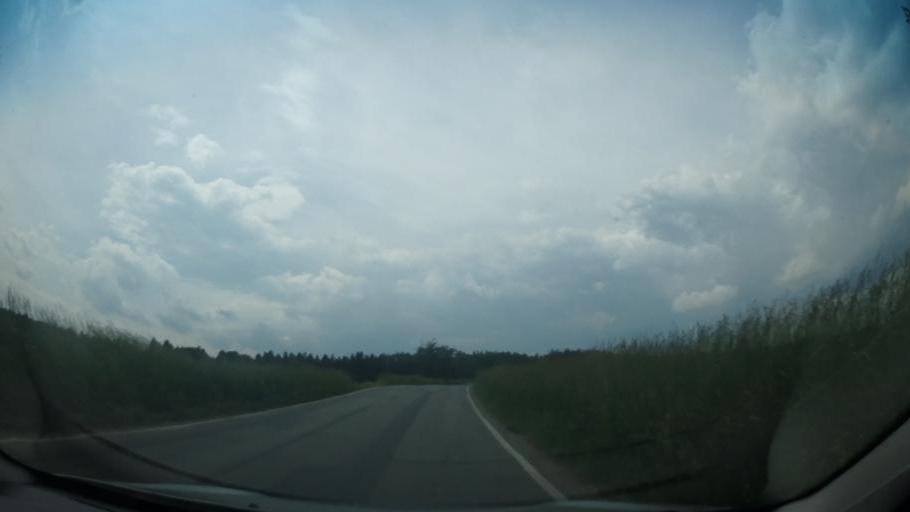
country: CZ
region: South Moravian
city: Lysice
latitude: 49.4545
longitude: 16.5005
